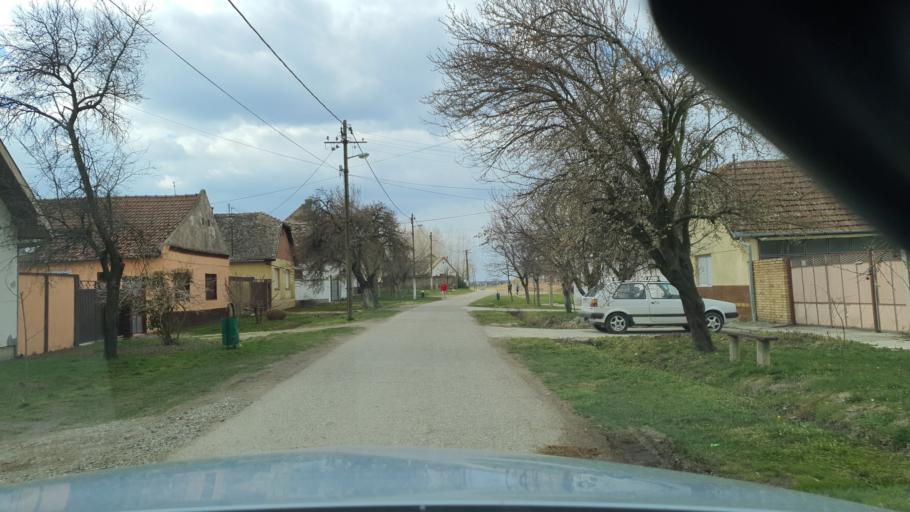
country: RS
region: Autonomna Pokrajina Vojvodina
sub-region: Juznobacki Okrug
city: Bac
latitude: 45.3920
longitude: 19.2228
